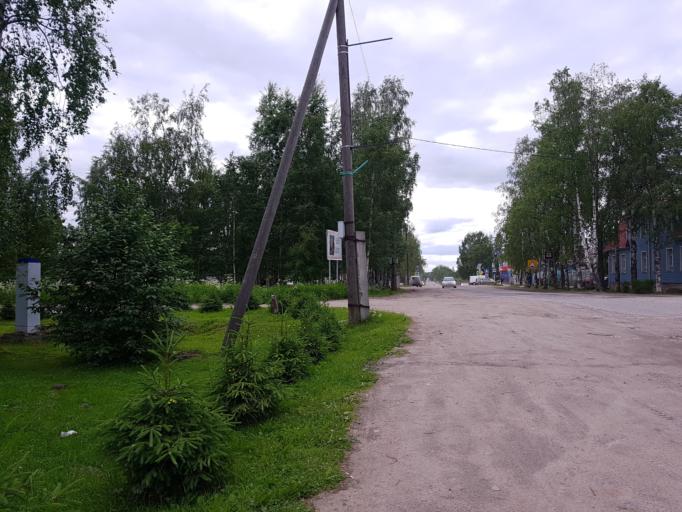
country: RU
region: Republic of Karelia
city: Kalevala
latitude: 65.1968
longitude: 31.1818
